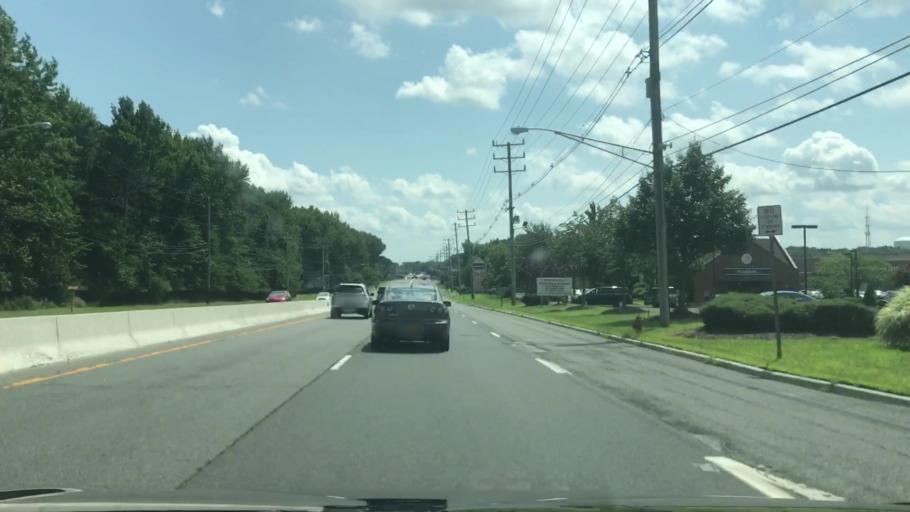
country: US
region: New Jersey
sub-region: Monmouth County
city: Wanamassa
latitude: 40.2506
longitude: -74.0392
